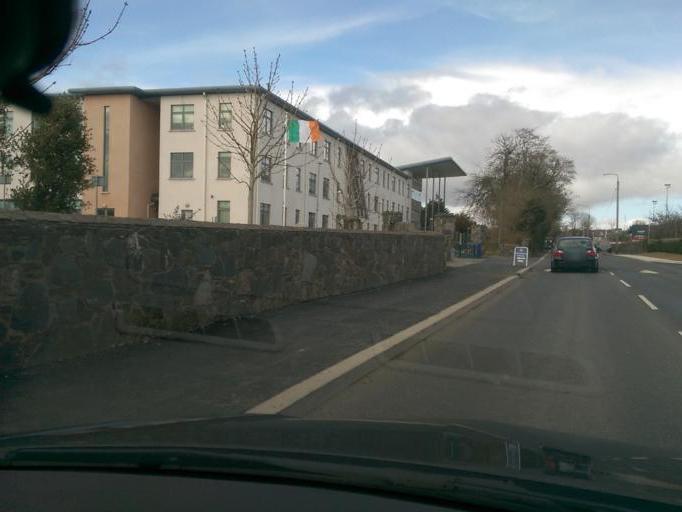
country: IE
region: Leinster
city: Malahide
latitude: 53.4375
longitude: -6.1520
